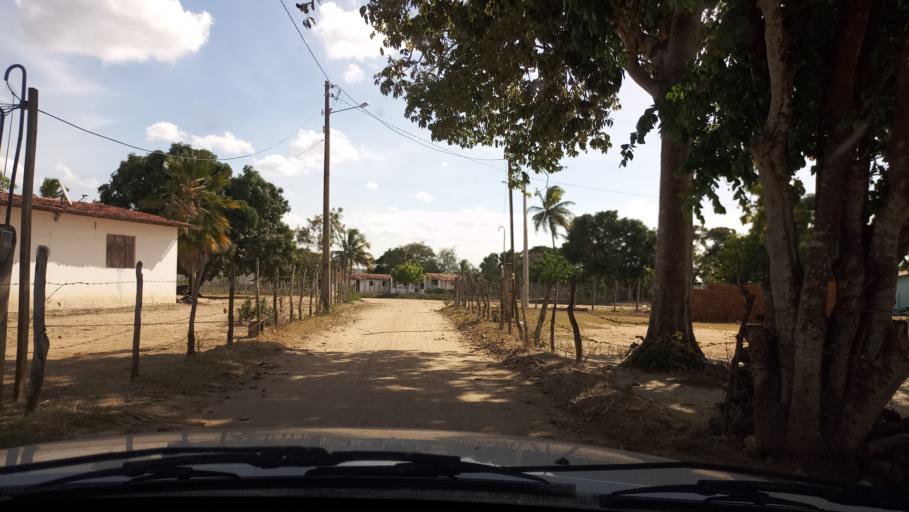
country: BR
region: Rio Grande do Norte
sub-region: Goianinha
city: Goianinha
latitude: -6.3191
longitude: -35.3084
